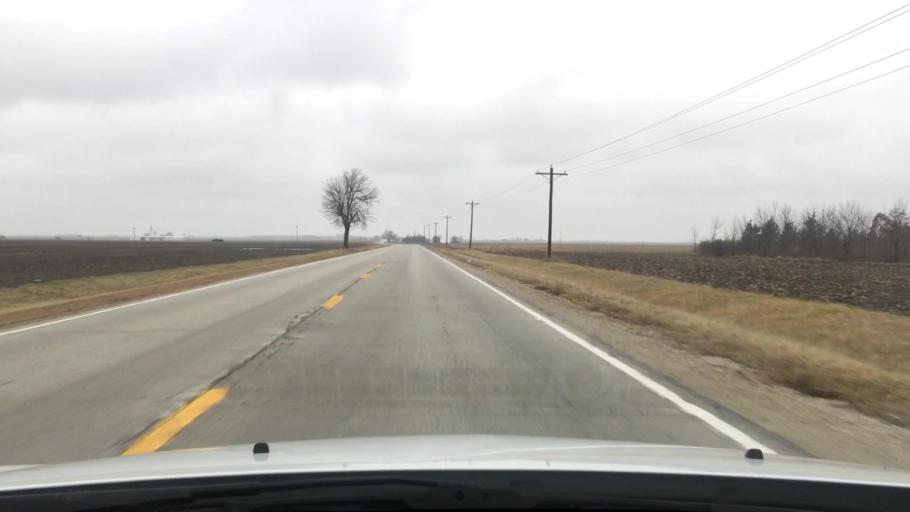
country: US
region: Illinois
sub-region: Iroquois County
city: Clifton
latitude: 40.8870
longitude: -87.8784
